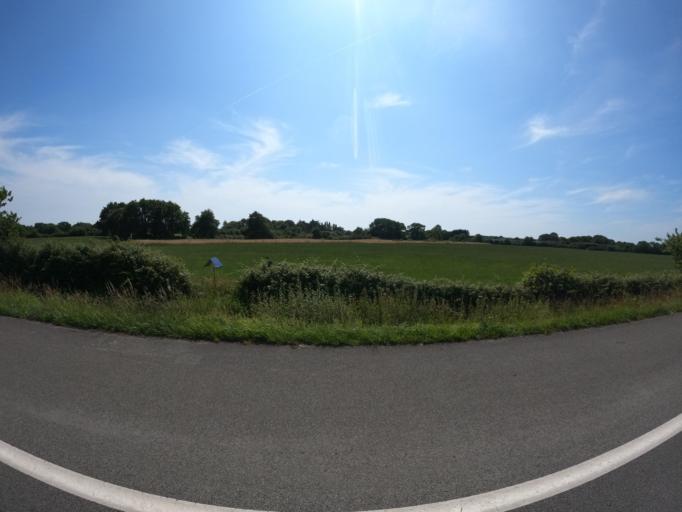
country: FR
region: Pays de la Loire
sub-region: Departement de la Loire-Atlantique
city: Pornic
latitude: 47.1321
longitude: -2.1210
